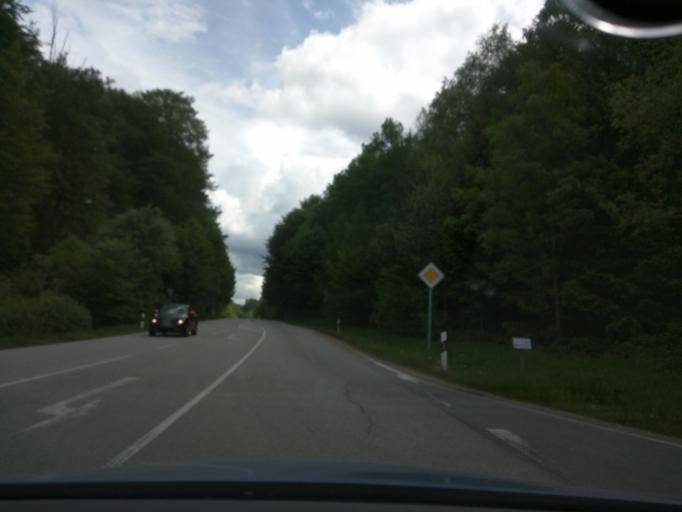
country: DE
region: Bavaria
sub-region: Lower Bavaria
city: Passau
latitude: 48.5340
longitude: 13.3905
